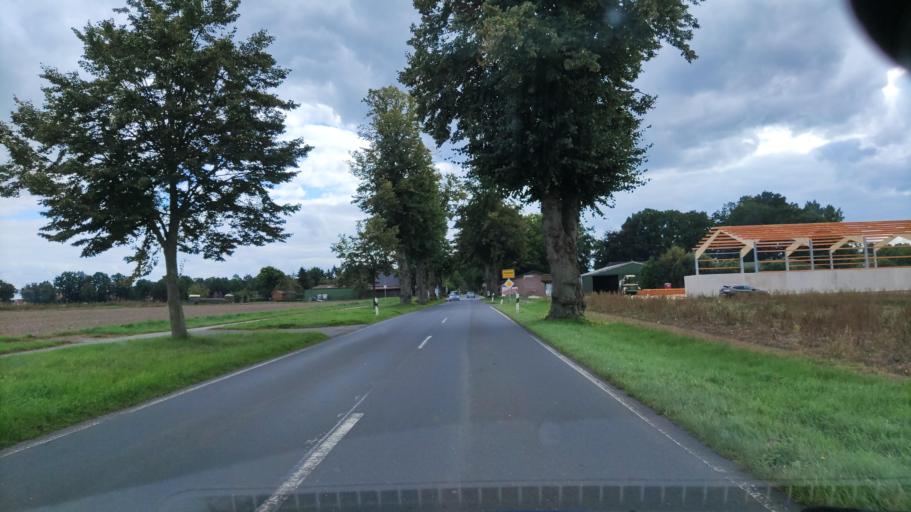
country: DE
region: Lower Saxony
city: Tostedt
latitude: 53.2874
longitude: 9.7134
